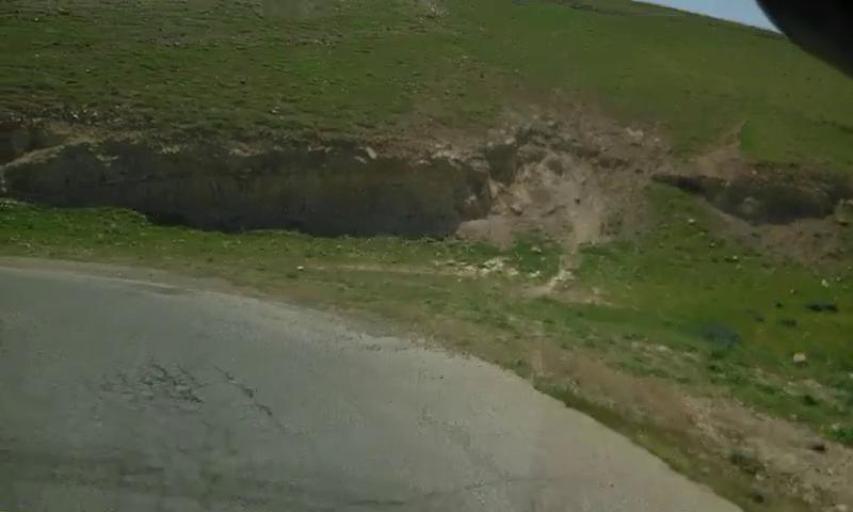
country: PS
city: `Arab ar Rashaydah
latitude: 31.5558
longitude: 35.2477
